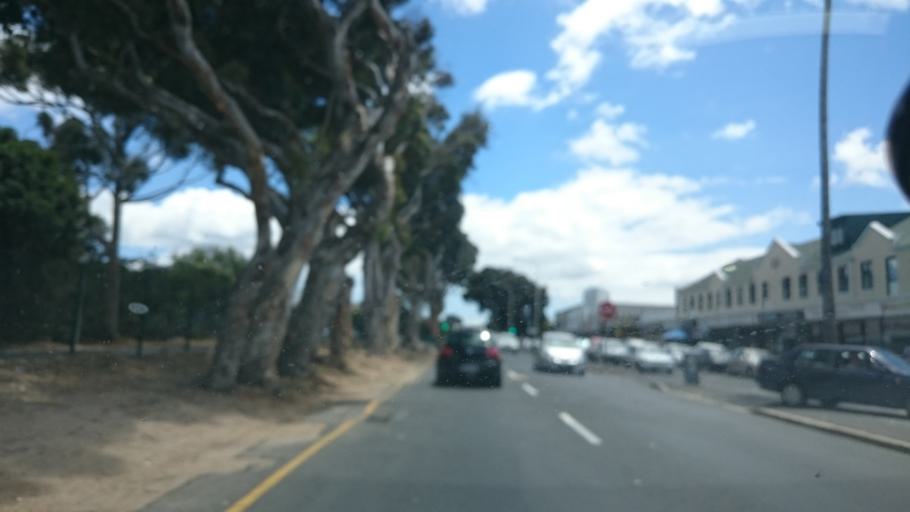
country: ZA
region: Western Cape
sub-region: City of Cape Town
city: Bergvliet
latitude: -34.0456
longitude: 18.4629
